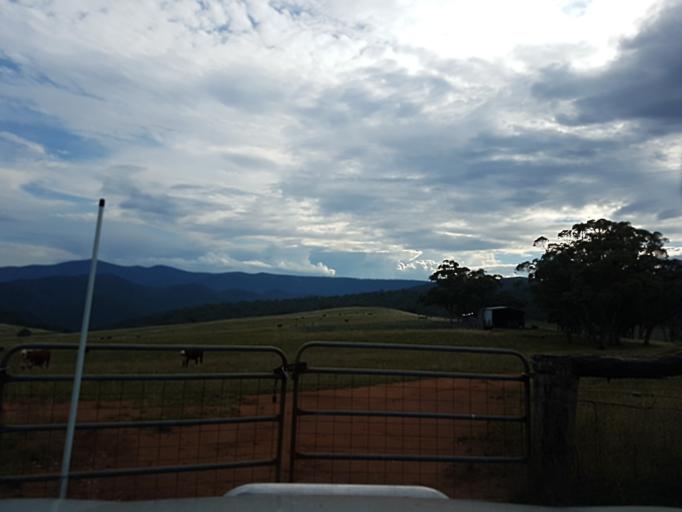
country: AU
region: New South Wales
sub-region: Snowy River
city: Jindabyne
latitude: -36.9607
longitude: 148.3778
